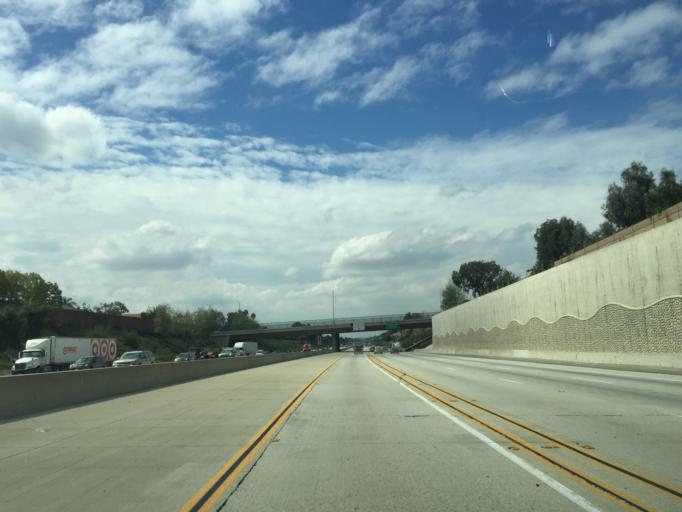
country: US
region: California
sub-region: Los Angeles County
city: Claremont
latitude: 34.1201
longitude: -117.7048
